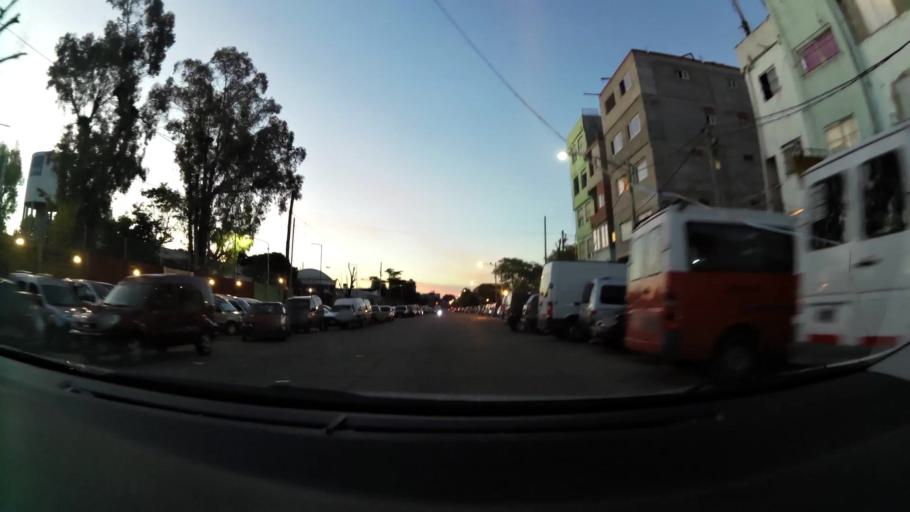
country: AR
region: Buenos Aires F.D.
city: Villa Lugano
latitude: -34.6494
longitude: -58.4465
